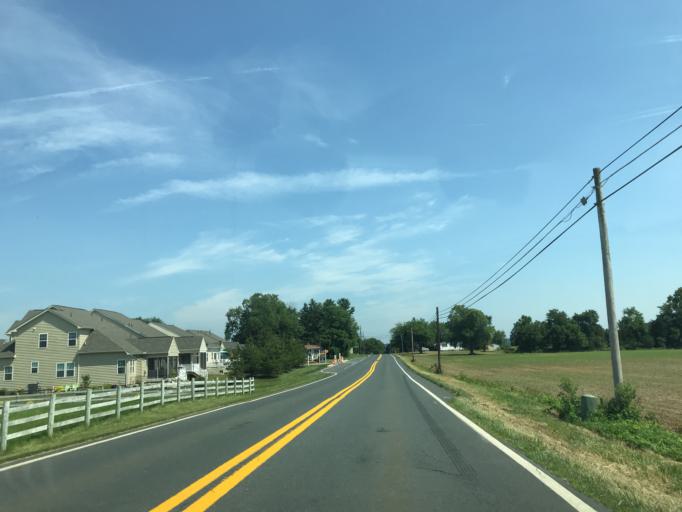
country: US
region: Maryland
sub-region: Carroll County
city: Taneytown
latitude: 39.6391
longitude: -77.1592
